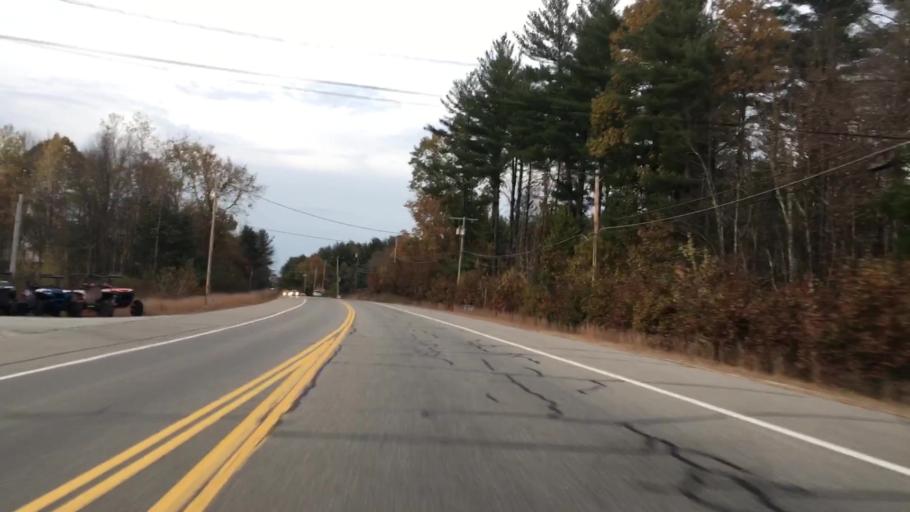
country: US
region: New Hampshire
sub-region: Hillsborough County
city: Milford
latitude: 42.8199
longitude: -71.6457
